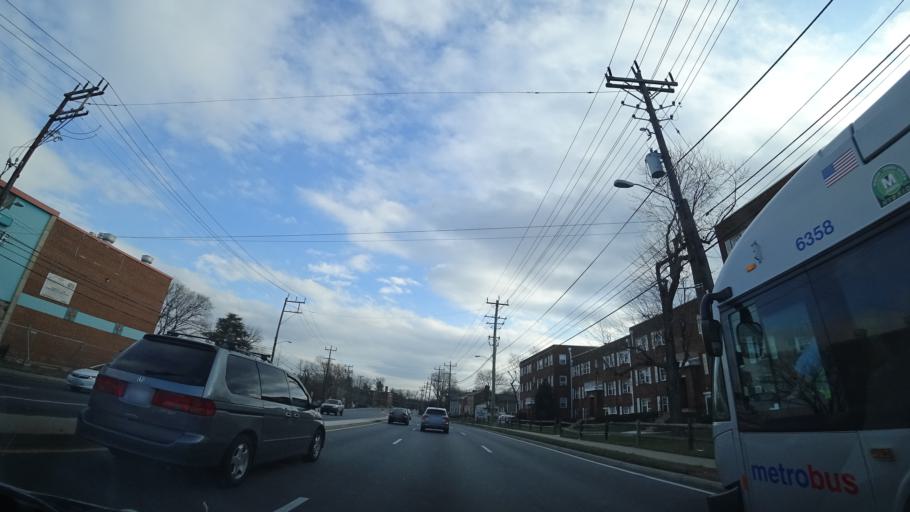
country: US
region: Maryland
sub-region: Prince George's County
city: Langley Park
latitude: 38.9990
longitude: -76.9952
